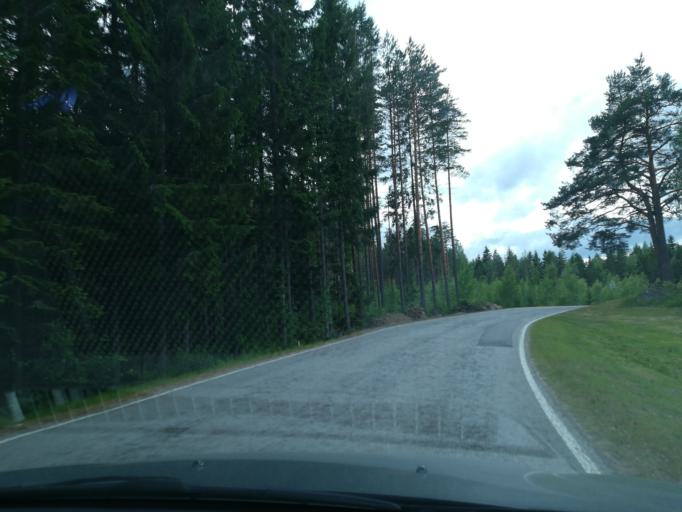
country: FI
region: South Karelia
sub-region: Lappeenranta
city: Savitaipale
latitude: 61.2614
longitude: 27.7112
